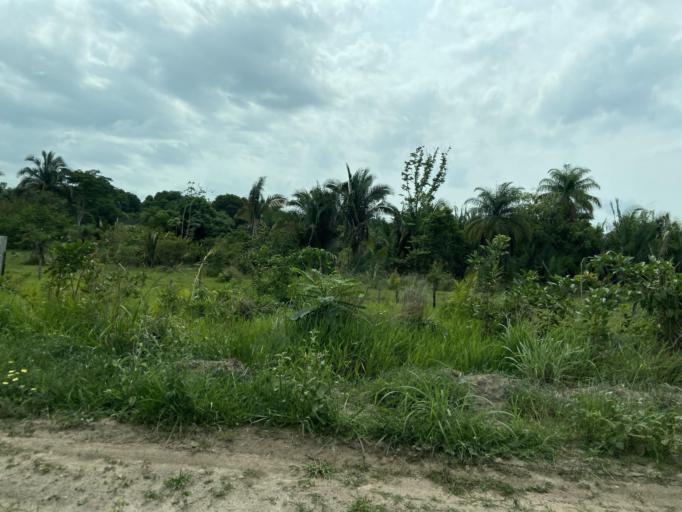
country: BR
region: Para
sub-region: Maraba
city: Maraba
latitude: -5.2949
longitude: -49.0651
